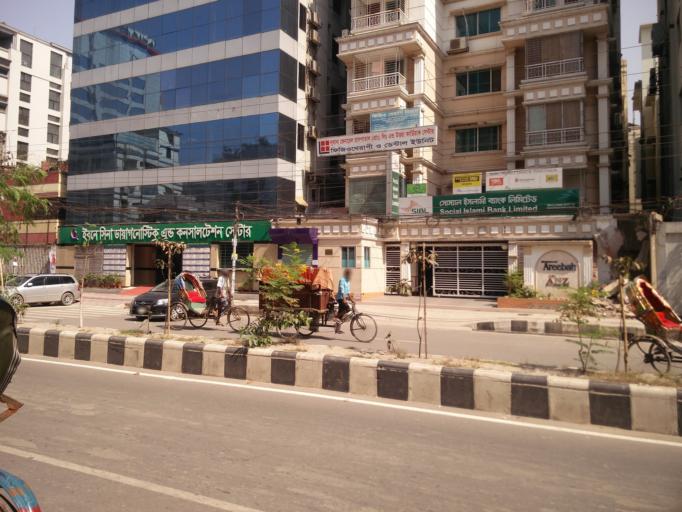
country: BD
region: Dhaka
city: Tungi
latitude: 23.8730
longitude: 90.3909
